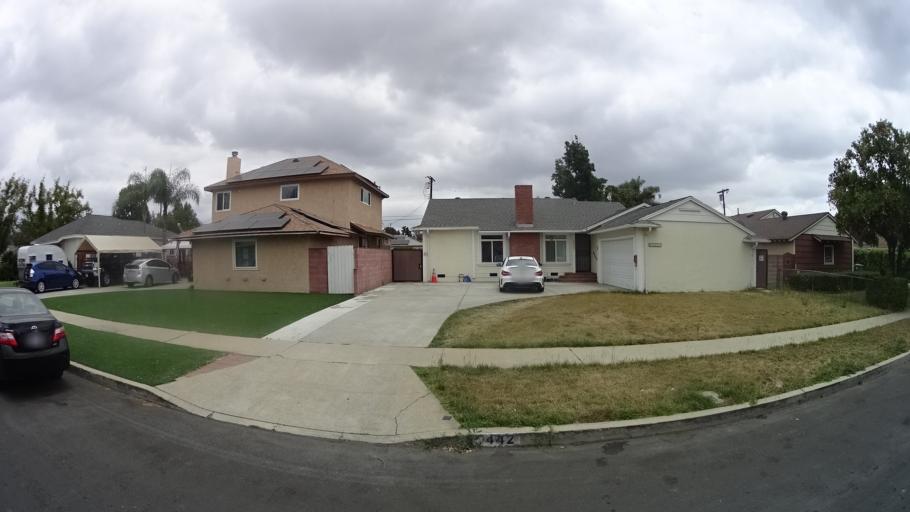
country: US
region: California
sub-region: Los Angeles County
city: San Fernando
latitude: 34.2604
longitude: -118.4651
